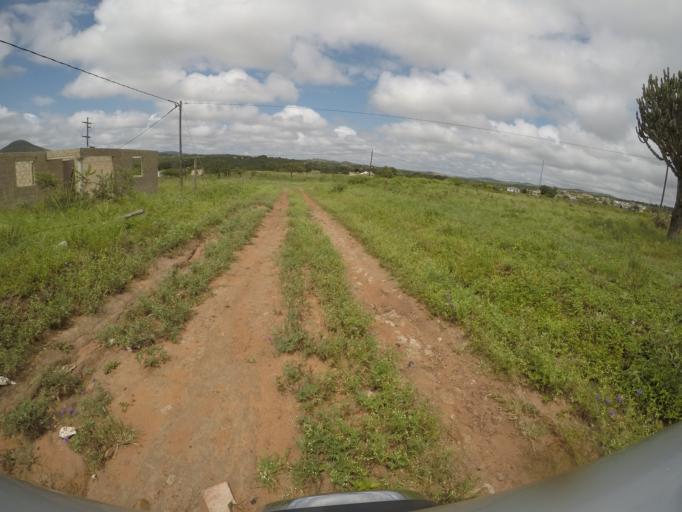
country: ZA
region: KwaZulu-Natal
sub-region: uThungulu District Municipality
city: Empangeni
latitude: -28.5845
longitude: 31.8485
